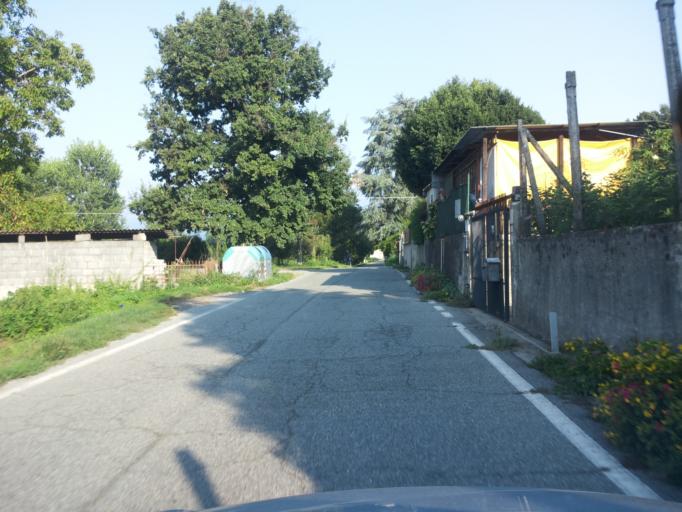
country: IT
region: Piedmont
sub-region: Provincia di Torino
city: Palazzo Canavese
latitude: 45.4622
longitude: 7.9702
